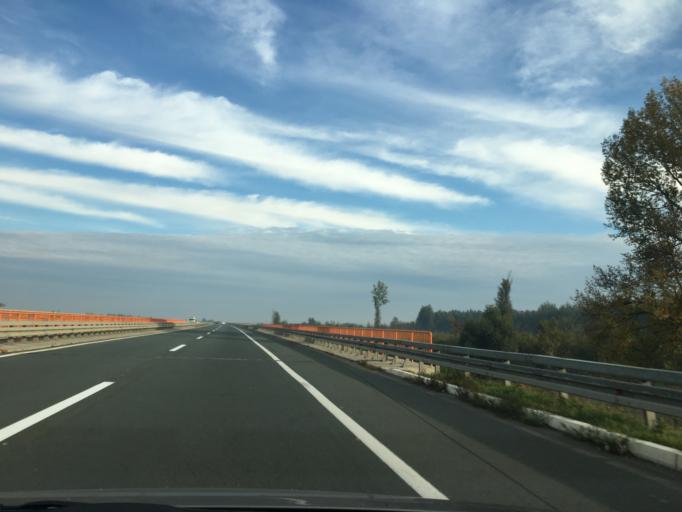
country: RS
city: Gardinovci
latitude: 45.1916
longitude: 20.0760
